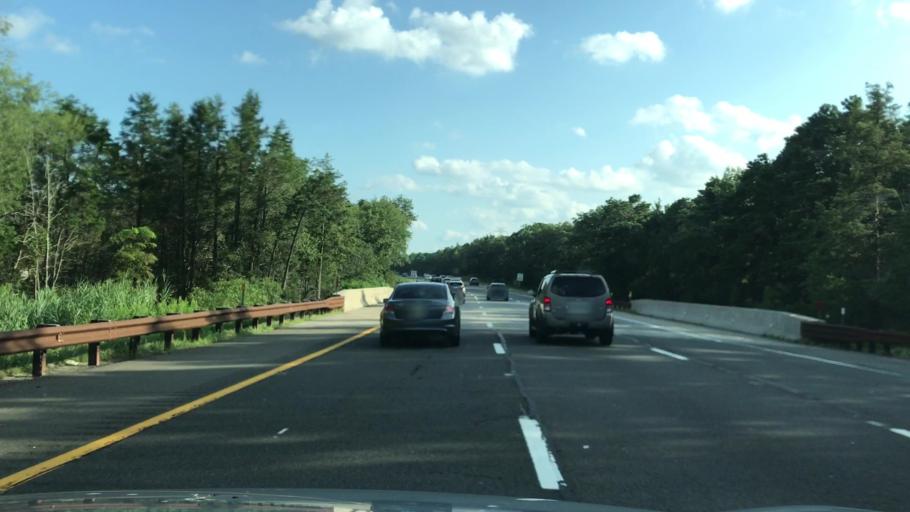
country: US
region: New Jersey
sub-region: Ocean County
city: Forked River
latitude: 39.8583
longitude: -74.2226
